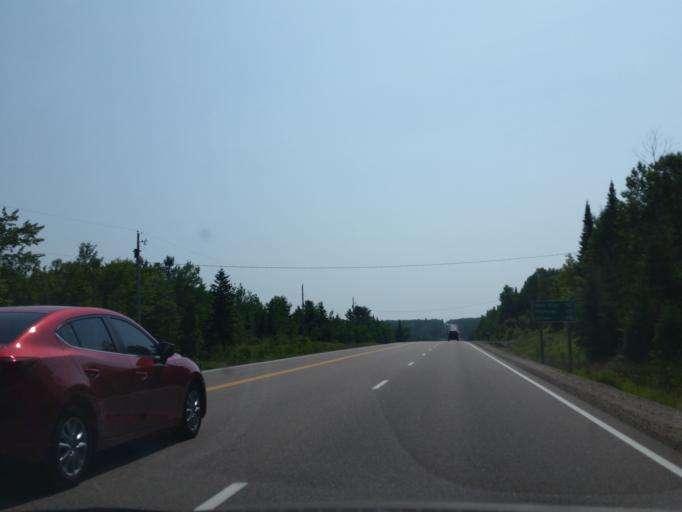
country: CA
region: Ontario
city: Mattawa
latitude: 46.3136
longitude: -78.6807
